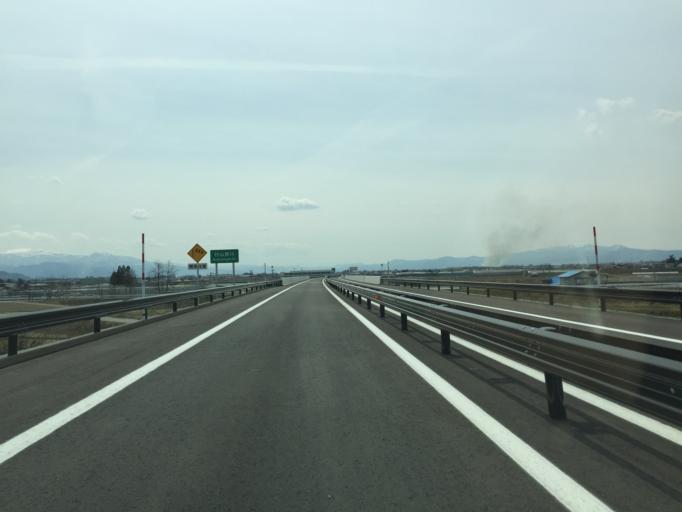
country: JP
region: Yamagata
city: Higashine
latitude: 38.4241
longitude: 140.3521
